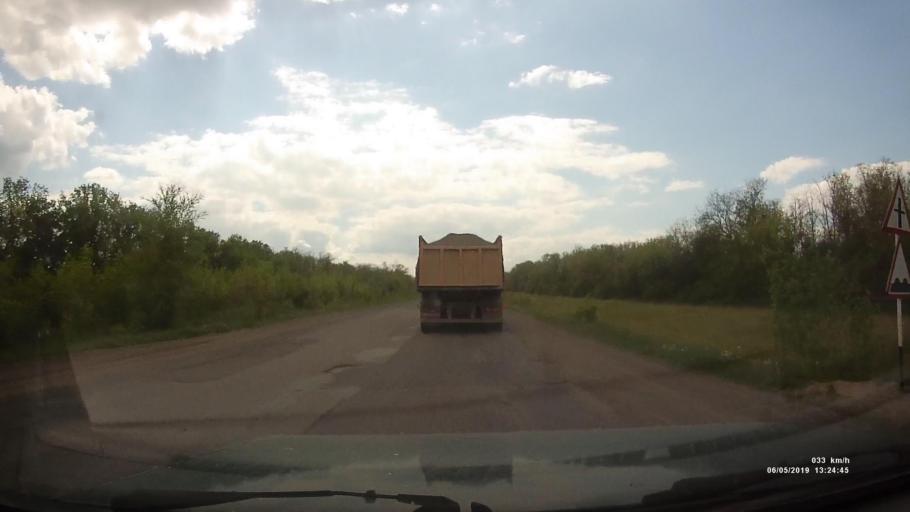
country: RU
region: Rostov
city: Ust'-Donetskiy
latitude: 47.6847
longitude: 40.9082
